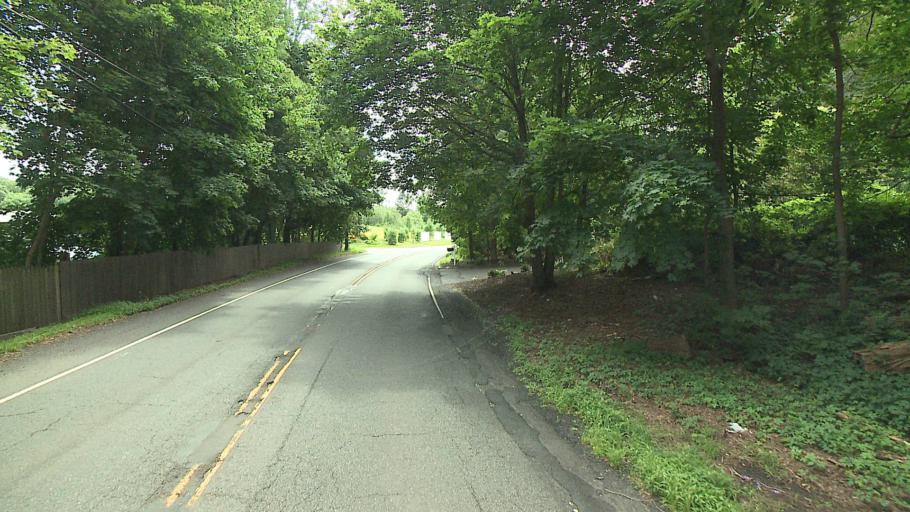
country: US
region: Connecticut
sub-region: Fairfield County
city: Danbury
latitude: 41.4255
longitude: -73.4829
